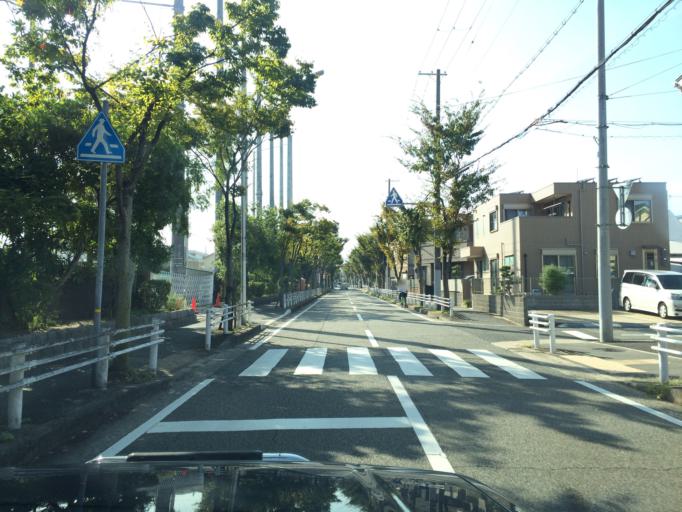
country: JP
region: Hyogo
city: Amagasaki
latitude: 34.7492
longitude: 135.4093
